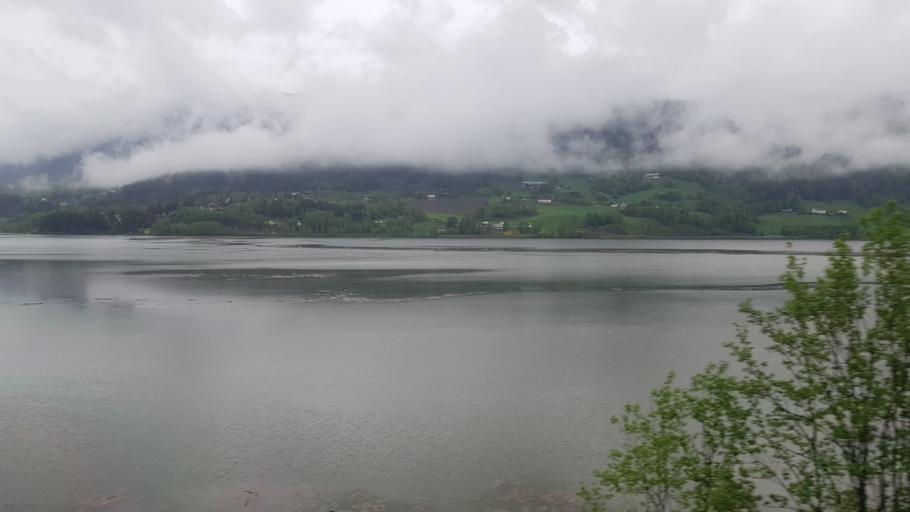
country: NO
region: Oppland
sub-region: Ringebu
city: Ringebu
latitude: 61.4273
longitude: 10.2056
